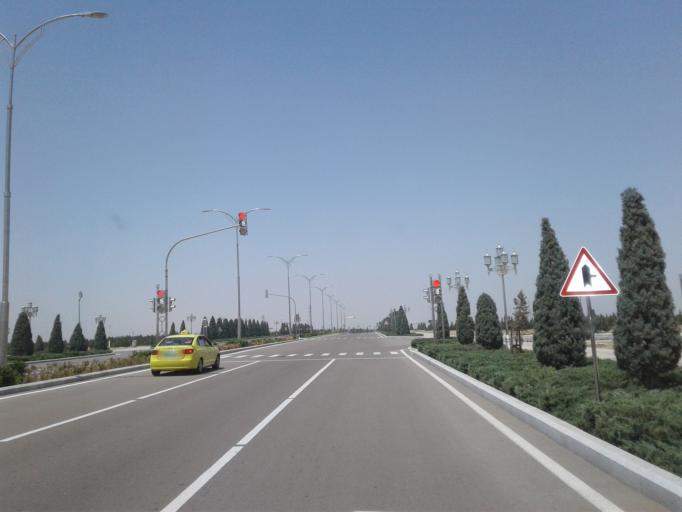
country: TM
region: Balkan
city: Turkmenbasy
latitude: 39.9620
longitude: 52.8646
